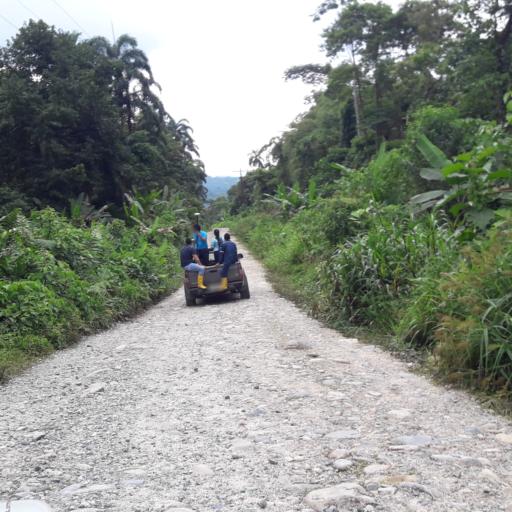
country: EC
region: Napo
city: Archidona
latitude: -0.9437
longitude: -77.8870
